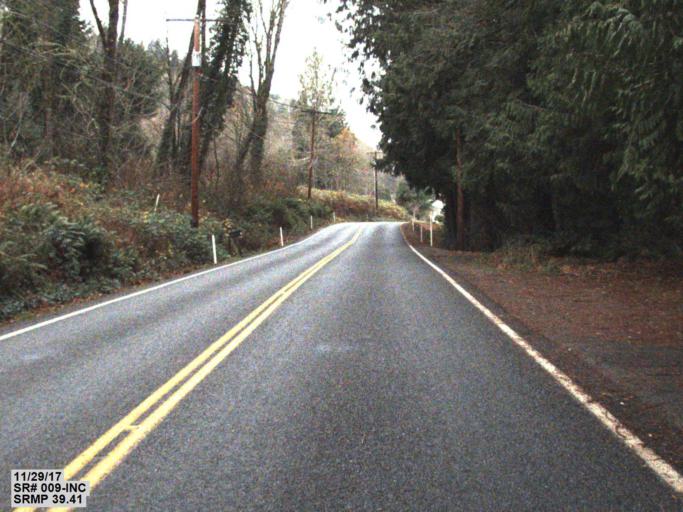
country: US
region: Washington
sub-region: Skagit County
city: Big Lake
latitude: 48.3103
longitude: -122.2265
